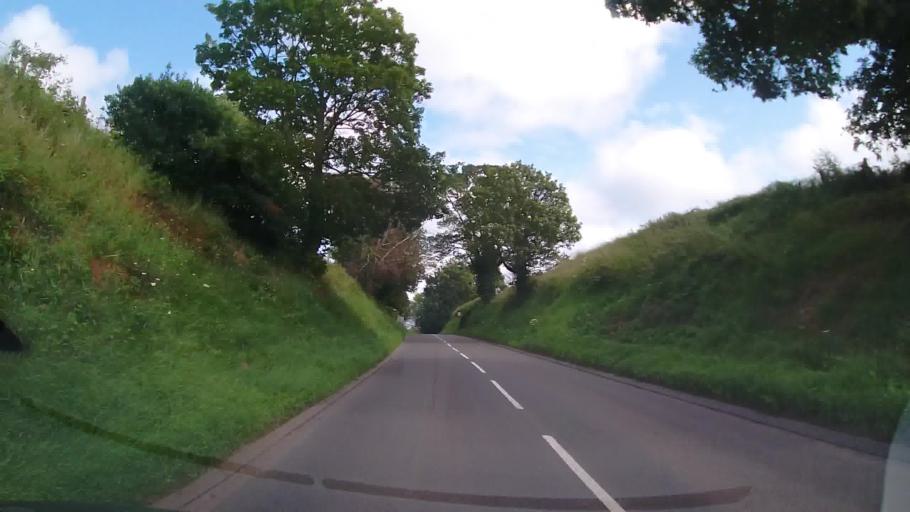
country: GB
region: England
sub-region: Shropshire
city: Pant
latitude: 52.7952
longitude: -2.9975
